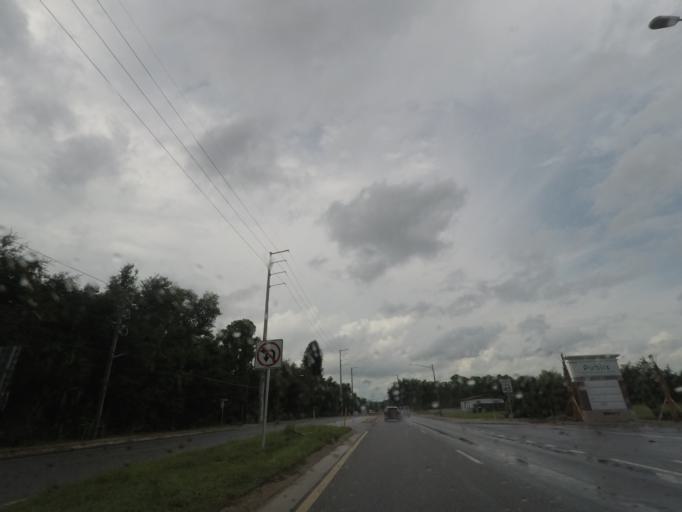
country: US
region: Florida
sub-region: Polk County
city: Loughman
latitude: 28.2381
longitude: -81.5605
